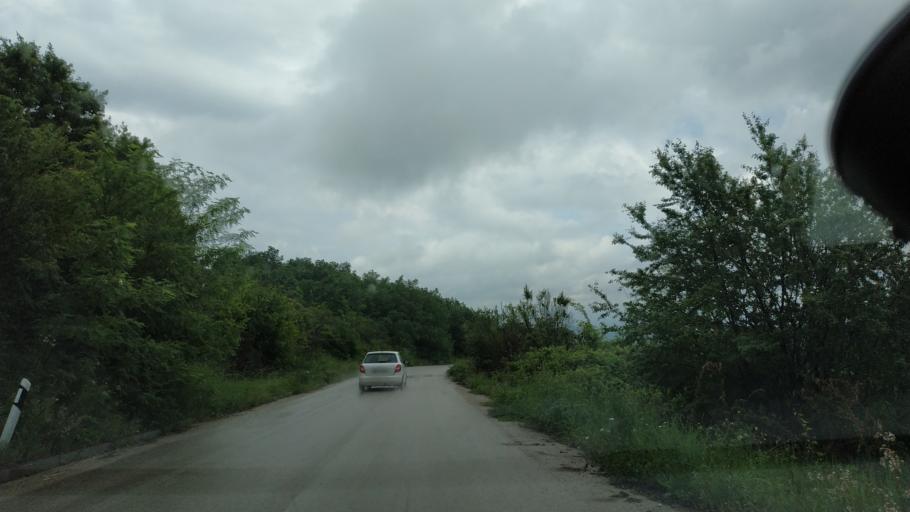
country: RS
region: Central Serbia
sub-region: Toplicki Okrug
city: Prokuplje
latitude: 43.4123
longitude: 21.5530
